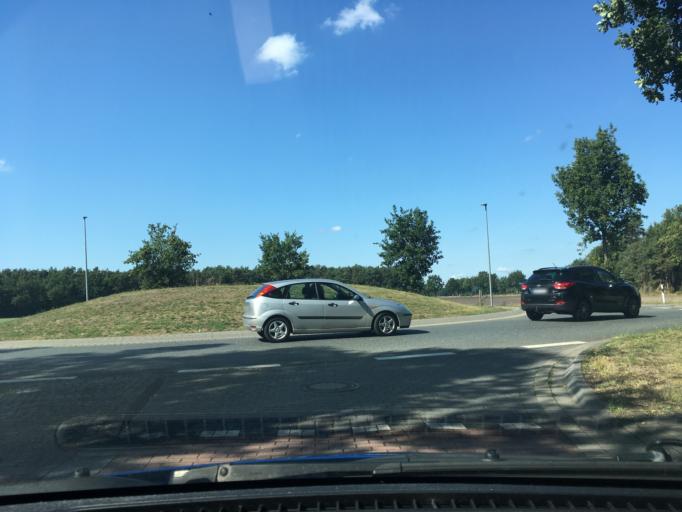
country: DE
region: Lower Saxony
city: Winsen
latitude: 52.6932
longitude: 9.9132
